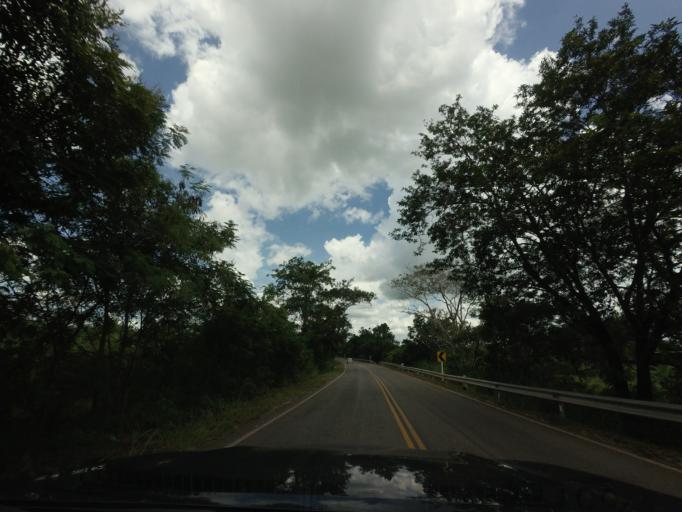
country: TH
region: Changwat Udon Thani
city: Phibun Rak
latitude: 17.6068
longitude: 103.0761
